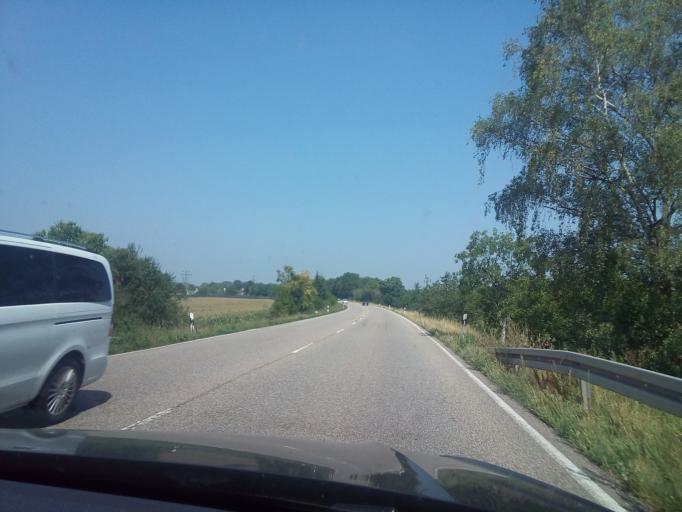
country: DE
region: Baden-Wuerttemberg
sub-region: Freiburg Region
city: Achern
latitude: 48.6333
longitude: 8.0499
